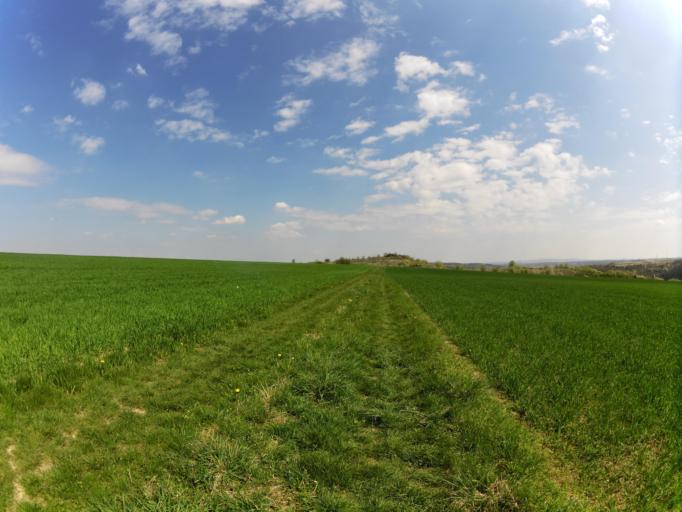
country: DE
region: Bavaria
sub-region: Regierungsbezirk Unterfranken
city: Winterhausen
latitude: 49.6809
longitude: 10.0099
